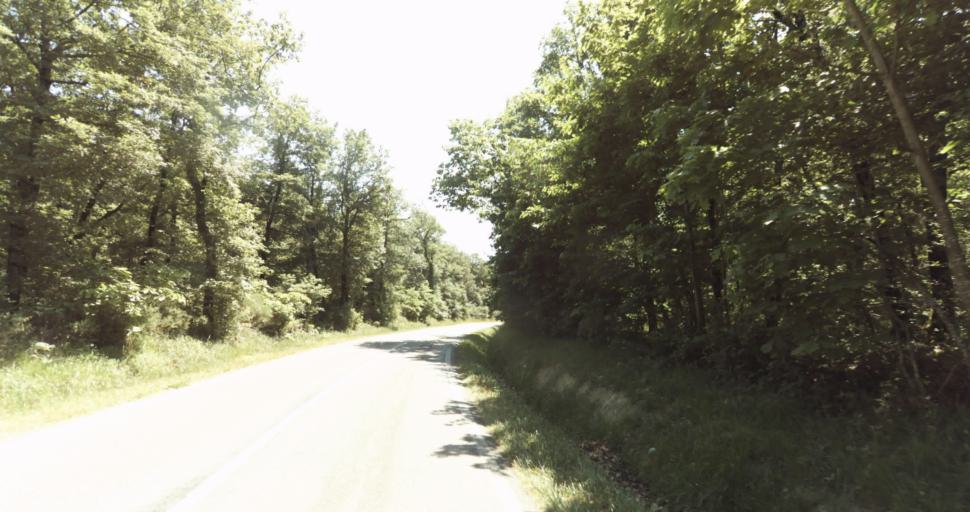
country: FR
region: Midi-Pyrenees
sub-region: Departement de la Haute-Garonne
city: Levignac
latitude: 43.6213
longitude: 1.1897
